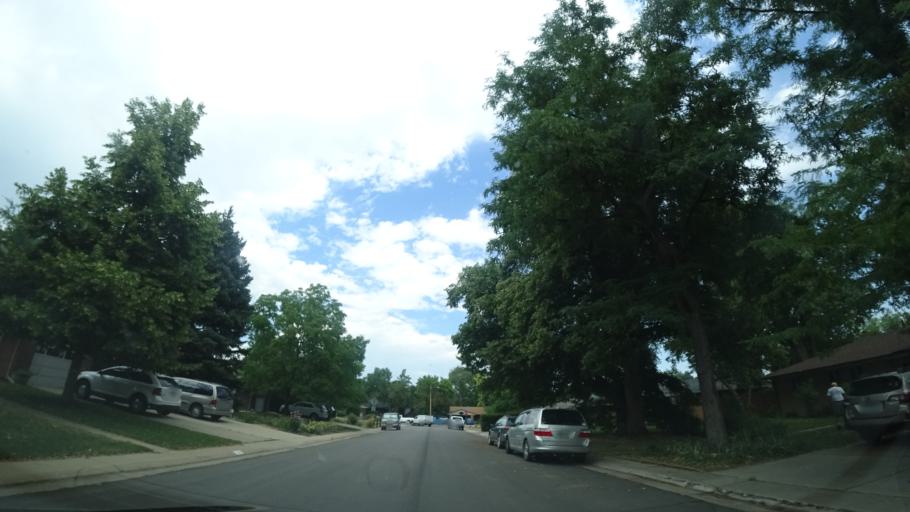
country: US
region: Colorado
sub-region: Jefferson County
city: Lakewood
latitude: 39.7190
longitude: -105.0991
